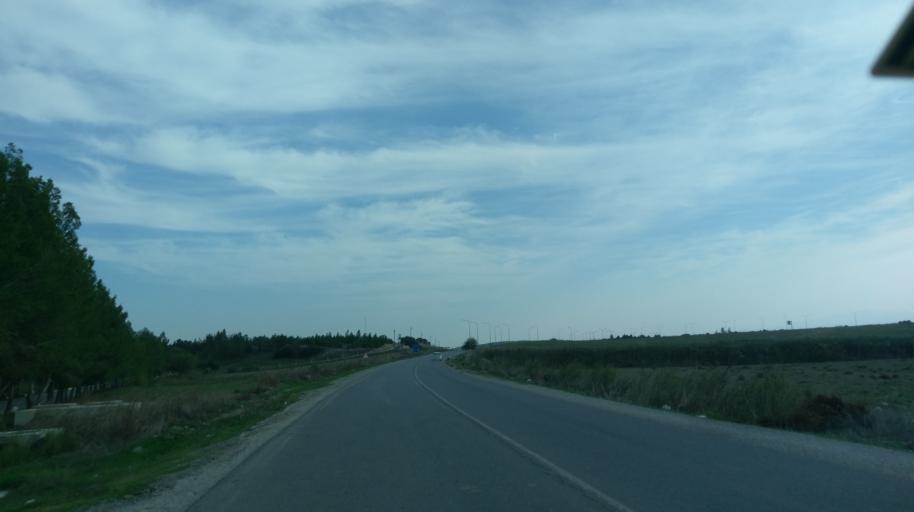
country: CY
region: Lefkosia
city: Mammari
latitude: 35.2217
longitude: 33.1780
